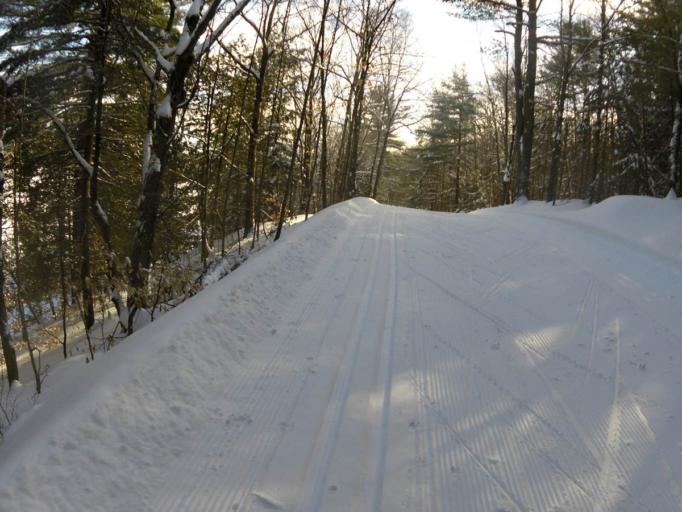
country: CA
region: Quebec
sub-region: Outaouais
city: Wakefield
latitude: 45.5976
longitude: -75.9951
